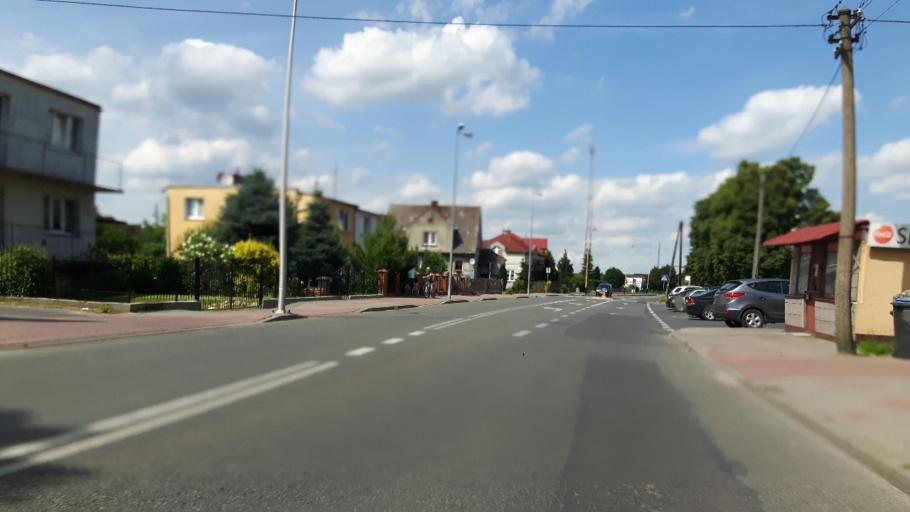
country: PL
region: West Pomeranian Voivodeship
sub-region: Powiat goleniowski
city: Nowogard
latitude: 53.6790
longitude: 15.1171
